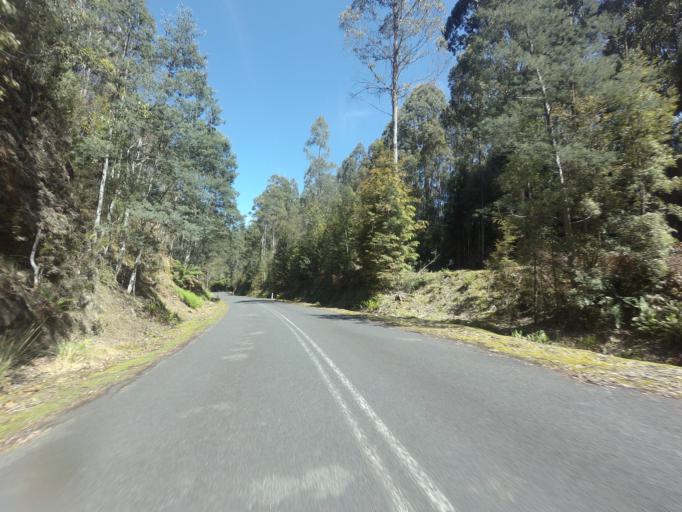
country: AU
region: Tasmania
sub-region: Huon Valley
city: Geeveston
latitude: -42.8193
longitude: 146.3420
